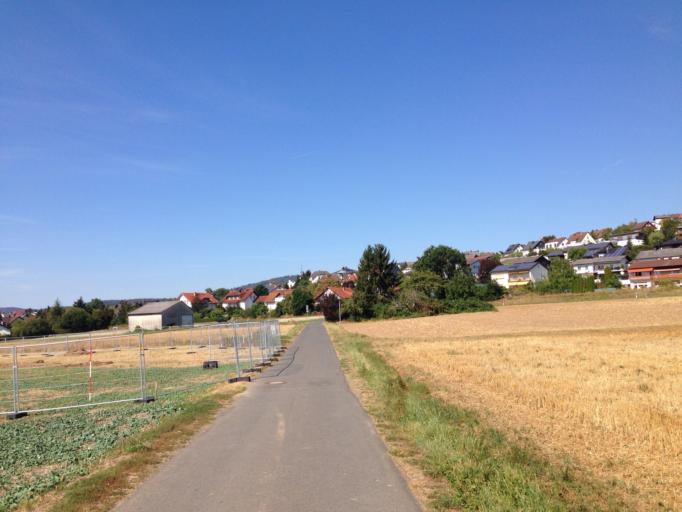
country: DE
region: Hesse
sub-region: Regierungsbezirk Giessen
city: Heuchelheim
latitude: 50.6153
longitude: 8.6149
